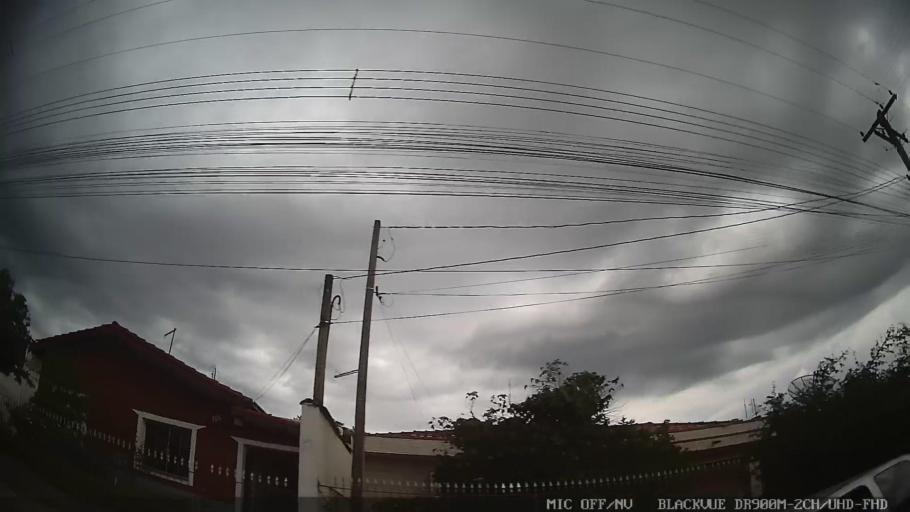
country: BR
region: Sao Paulo
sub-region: Amparo
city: Amparo
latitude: -22.7119
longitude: -46.8119
